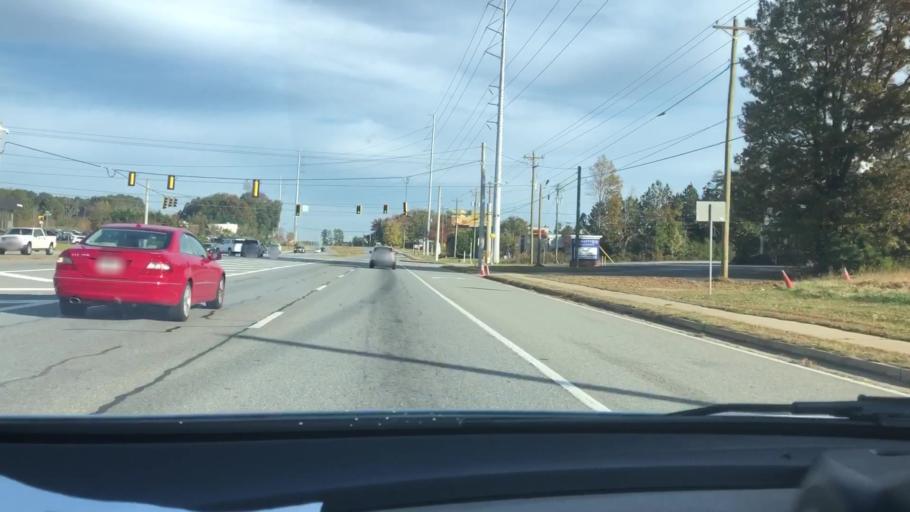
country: US
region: Georgia
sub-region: Forsyth County
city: Cumming
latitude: 34.1415
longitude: -84.1726
